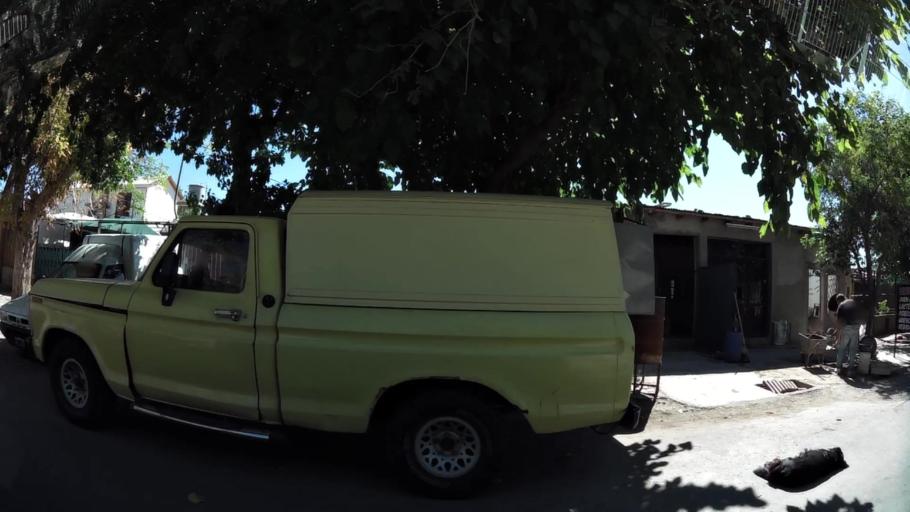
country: AR
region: Mendoza
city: Las Heras
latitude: -32.8304
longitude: -68.8223
